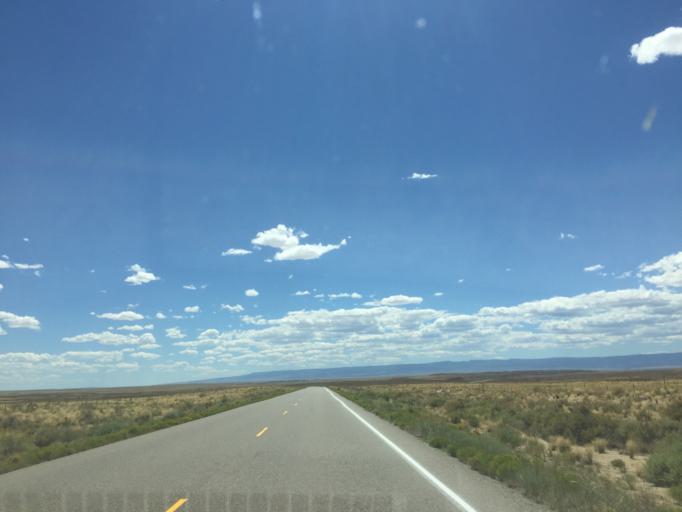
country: US
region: New Mexico
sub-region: San Juan County
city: Kirtland
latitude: 36.3882
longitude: -108.4848
